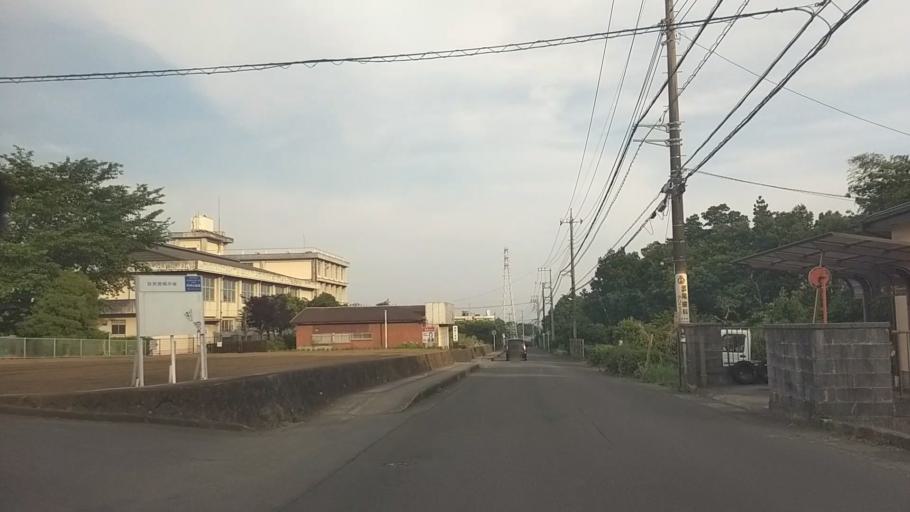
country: JP
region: Kanagawa
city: Odawara
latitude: 35.3218
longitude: 139.1109
